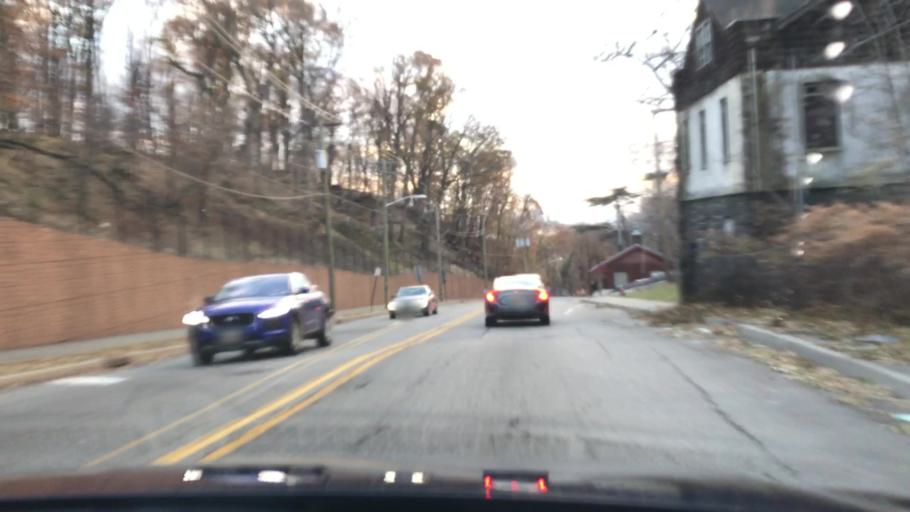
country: US
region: New Jersey
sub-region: Bergen County
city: Fort Lee
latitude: 40.8490
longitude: -73.9648
